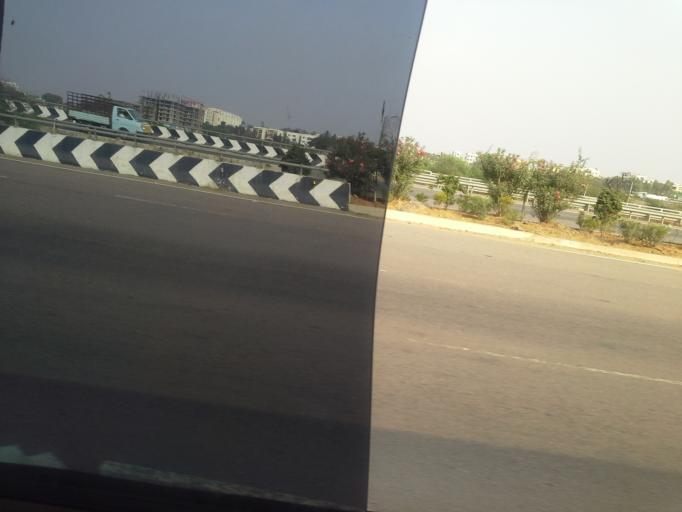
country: IN
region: Telangana
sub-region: Hyderabad
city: Hyderabad
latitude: 17.3919
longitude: 78.3517
